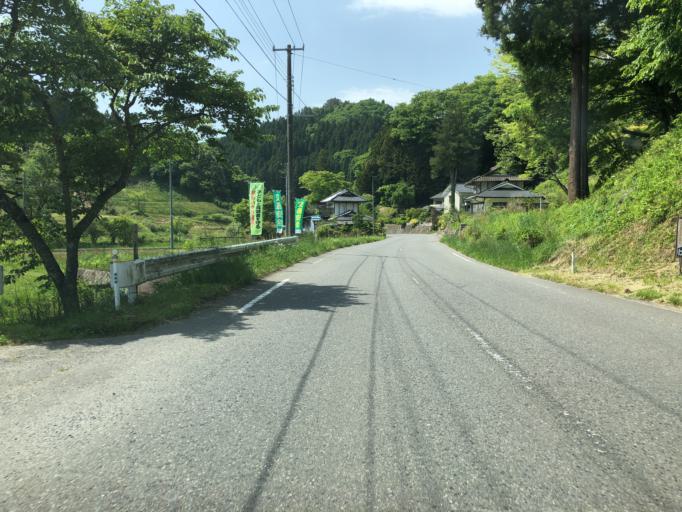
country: JP
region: Fukushima
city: Ishikawa
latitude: 37.1519
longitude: 140.4965
